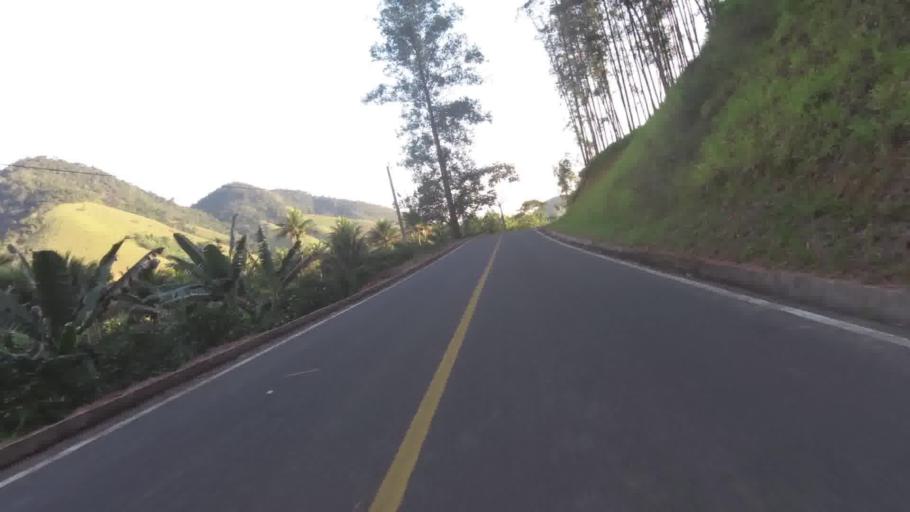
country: BR
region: Espirito Santo
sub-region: Alfredo Chaves
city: Alfredo Chaves
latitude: -20.5990
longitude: -40.7093
